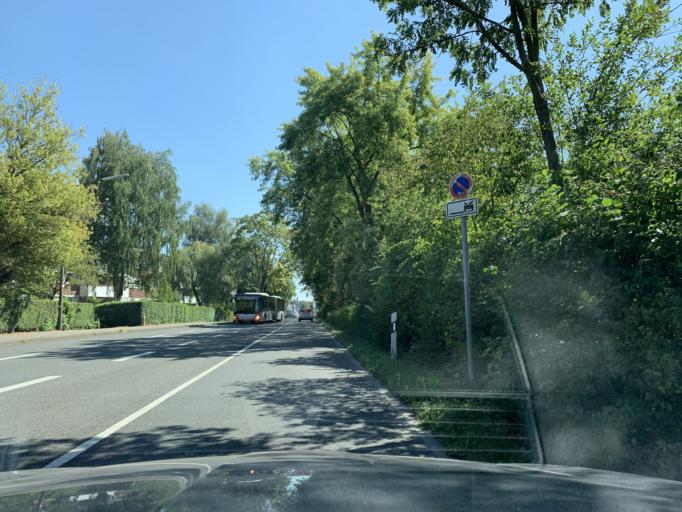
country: DE
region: North Rhine-Westphalia
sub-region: Regierungsbezirk Koln
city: Mengenich
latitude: 51.0025
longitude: 6.8757
